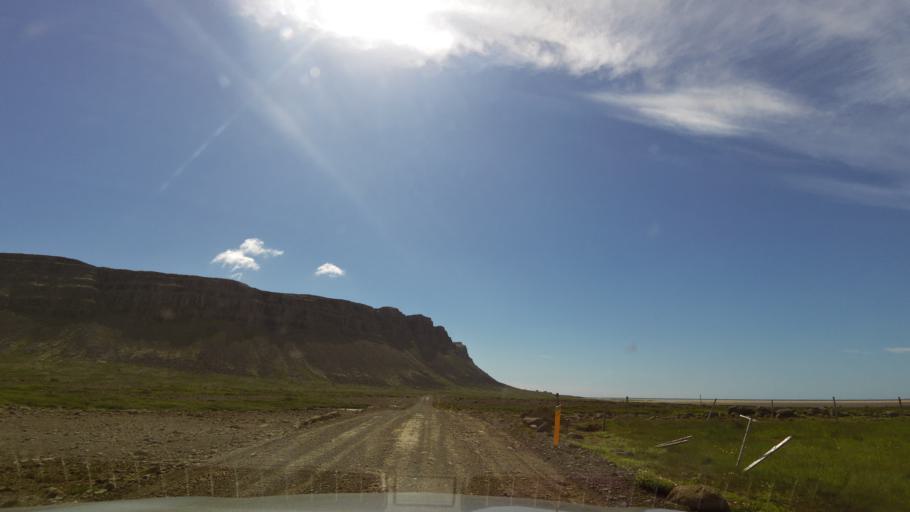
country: IS
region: West
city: Olafsvik
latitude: 65.4599
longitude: -23.9375
